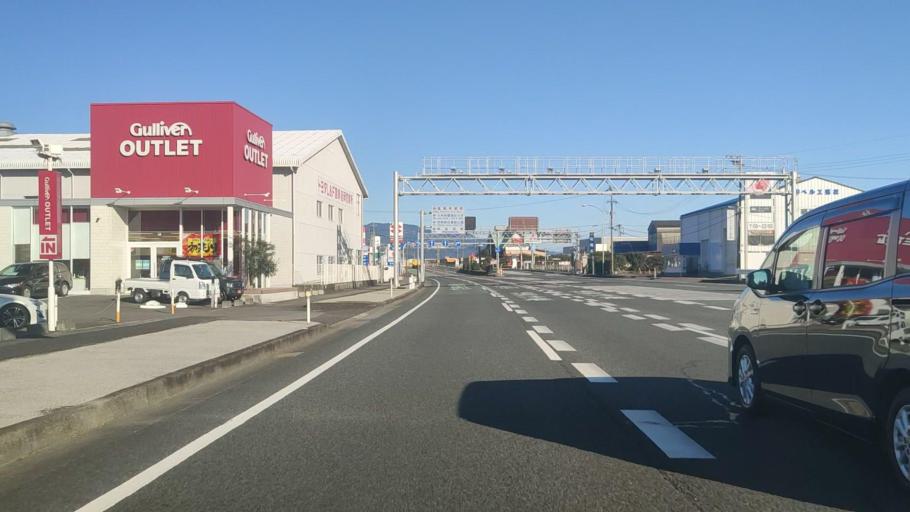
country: JP
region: Miyazaki
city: Nobeoka
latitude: 32.5424
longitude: 131.6783
